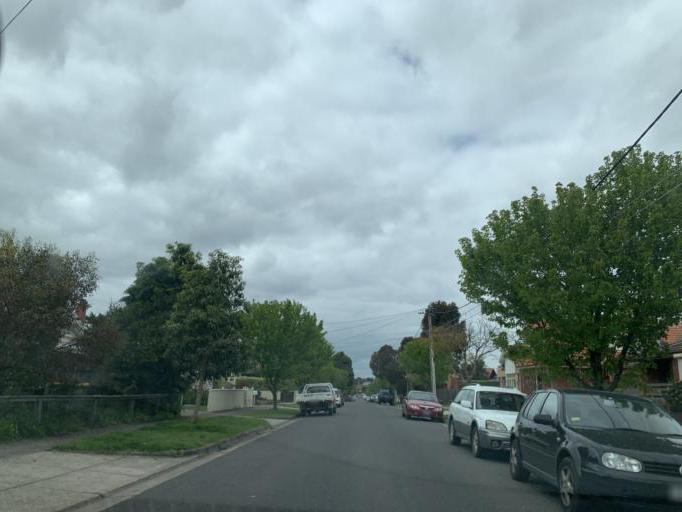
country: AU
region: Victoria
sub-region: Darebin
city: Reservoir
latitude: -37.7319
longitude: 144.9958
